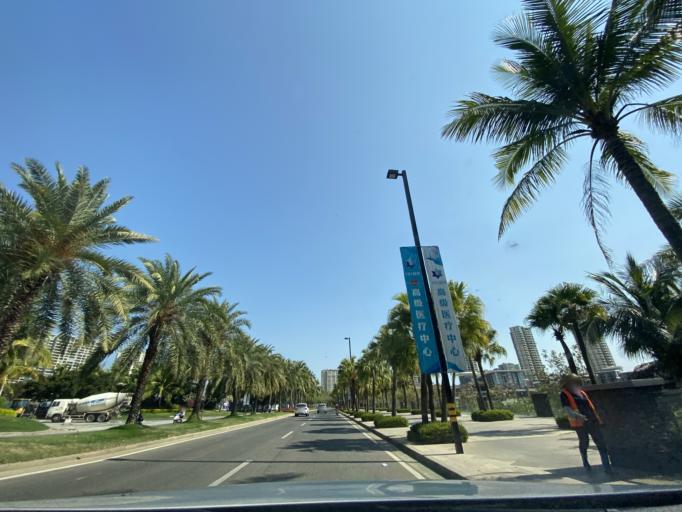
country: CN
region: Hainan
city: Yingzhou
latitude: 18.4083
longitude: 109.8713
